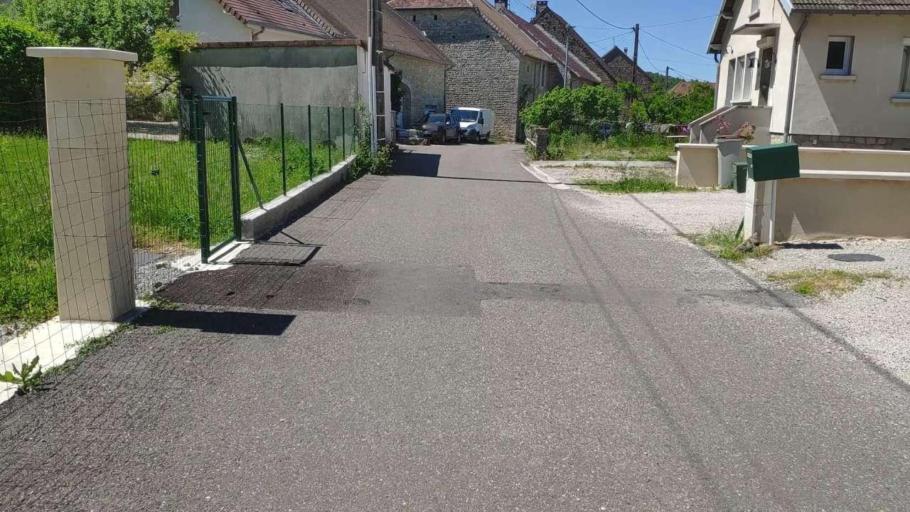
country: FR
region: Franche-Comte
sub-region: Departement du Jura
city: Perrigny
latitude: 46.7421
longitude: 5.6254
